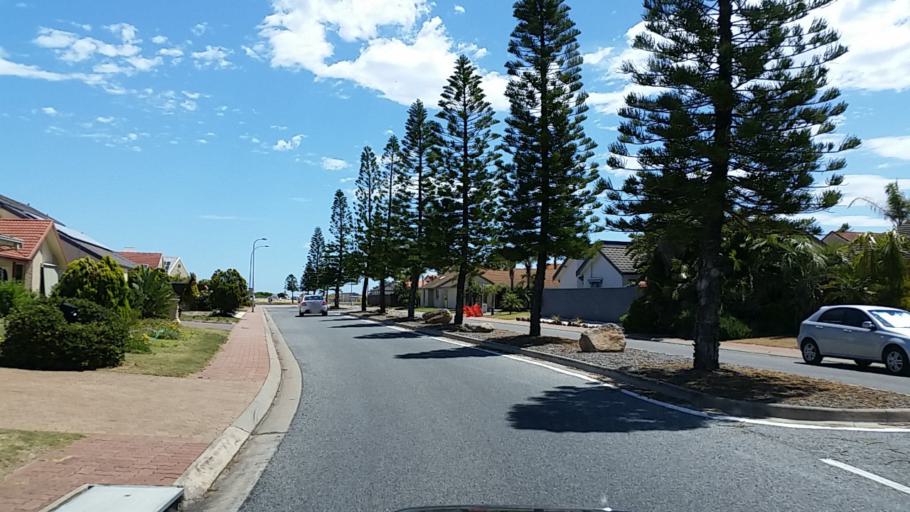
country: AU
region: South Australia
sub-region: Port Adelaide Enfield
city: Birkenhead
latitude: -34.7834
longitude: 138.4834
